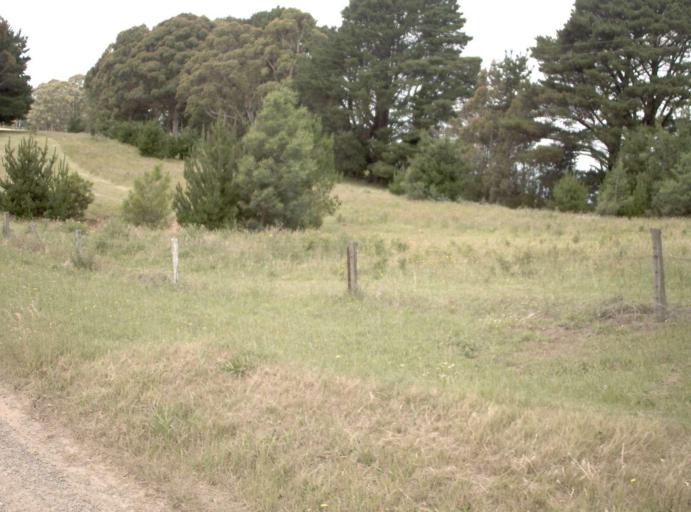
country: AU
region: Victoria
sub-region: Latrobe
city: Traralgon
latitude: -38.3727
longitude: 146.6878
